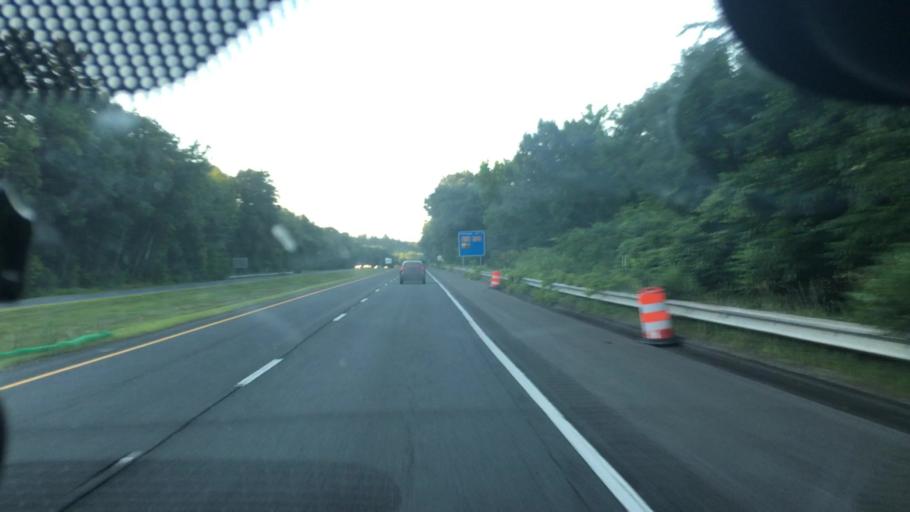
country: US
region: Massachusetts
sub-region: Franklin County
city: Greenfield
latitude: 42.5941
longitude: -72.6181
